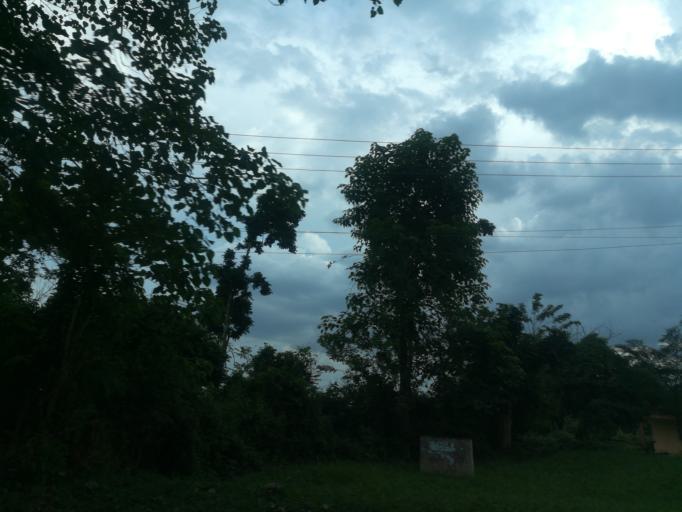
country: NG
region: Oyo
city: Ibadan
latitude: 7.4321
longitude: 3.8912
